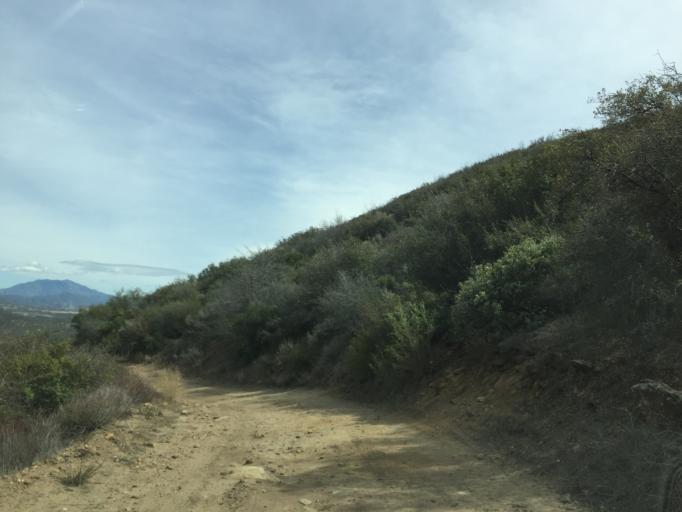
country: US
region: California
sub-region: Riverside County
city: Anza
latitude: 33.5960
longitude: -116.7799
